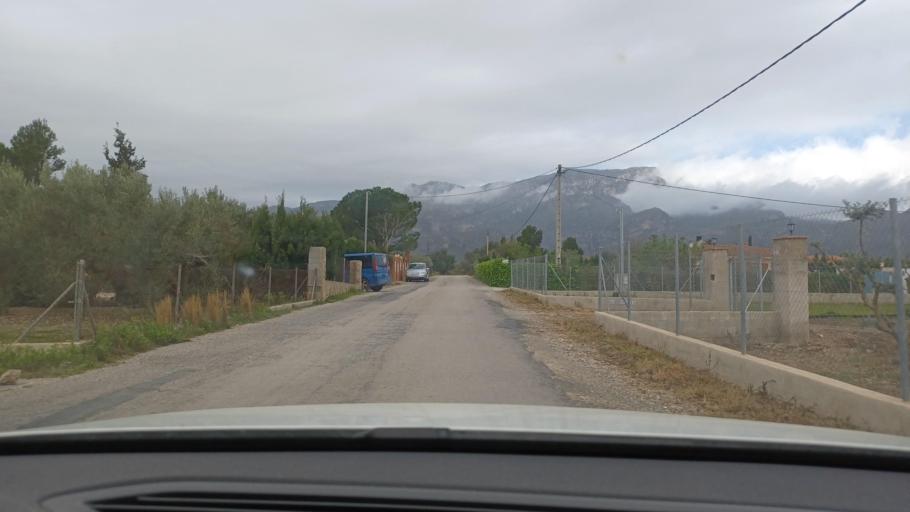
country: ES
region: Catalonia
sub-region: Provincia de Tarragona
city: Tortosa
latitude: 40.7963
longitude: 0.4344
